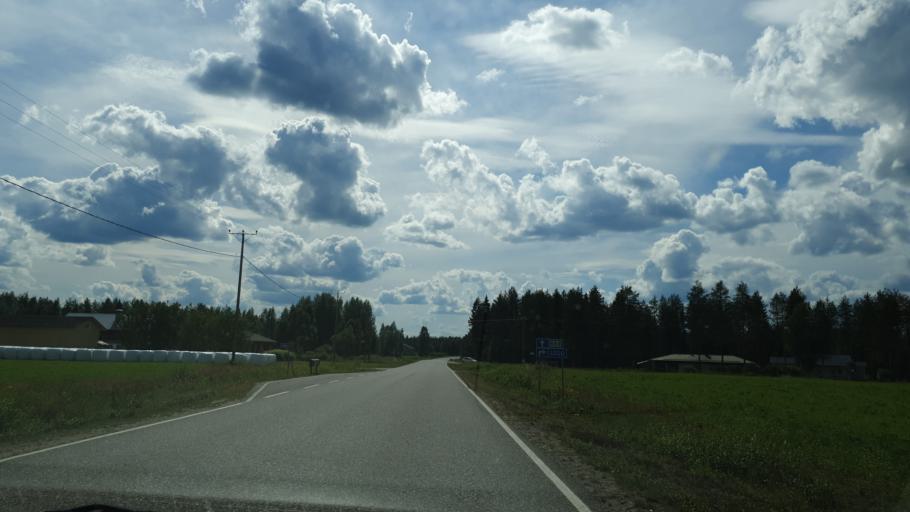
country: FI
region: Kainuu
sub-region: Kajaani
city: Sotkamo
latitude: 64.2315
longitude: 28.4985
